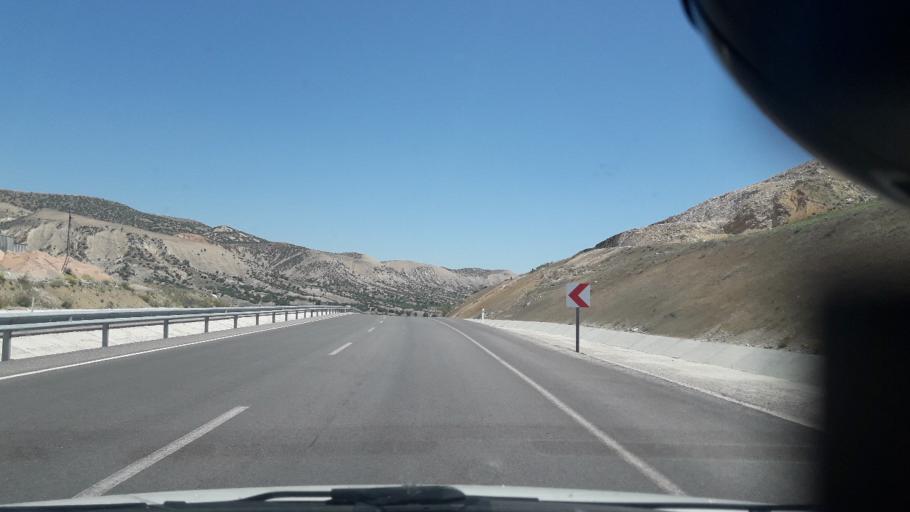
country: TR
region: Malatya
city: Hekimhan
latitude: 38.8082
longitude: 37.9530
